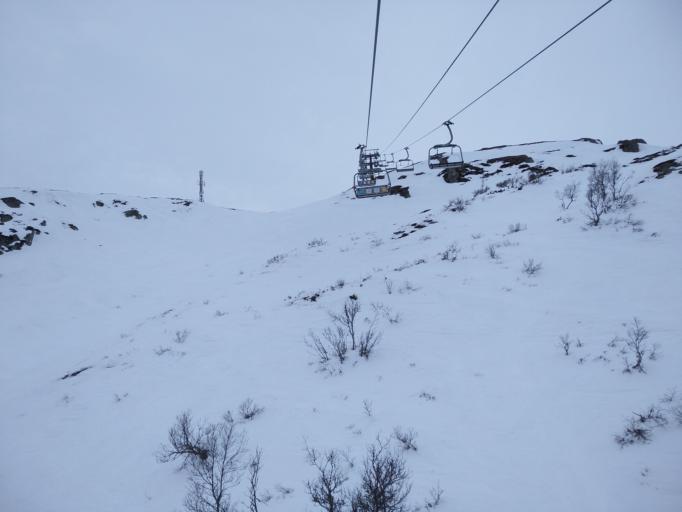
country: NO
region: Aust-Agder
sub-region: Bykle
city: Hovden
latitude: 59.5772
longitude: 7.3361
